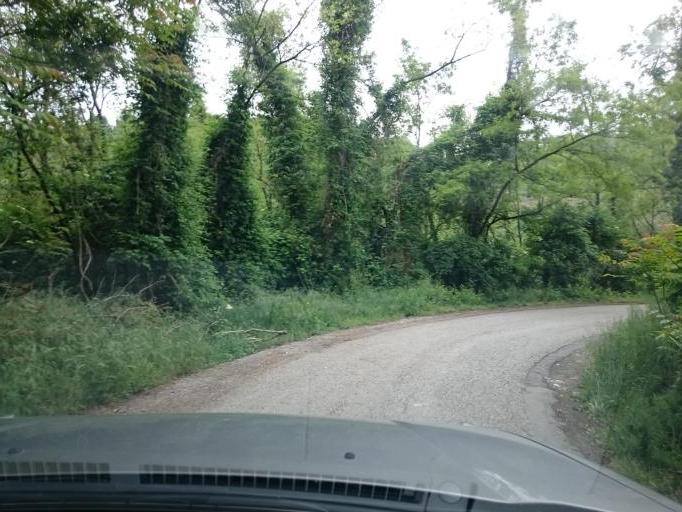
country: IT
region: Veneto
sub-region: Provincia di Padova
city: Baone
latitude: 45.2521
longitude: 11.6733
